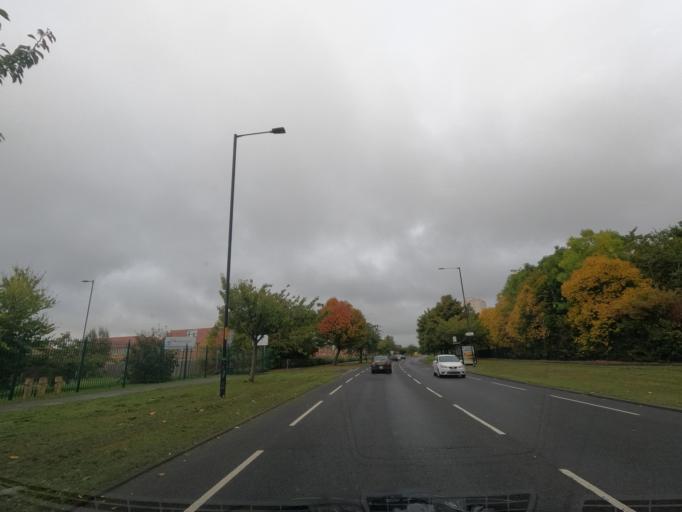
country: GB
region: England
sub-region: Middlesbrough
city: Nunthorpe
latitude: 54.5593
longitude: -1.1895
